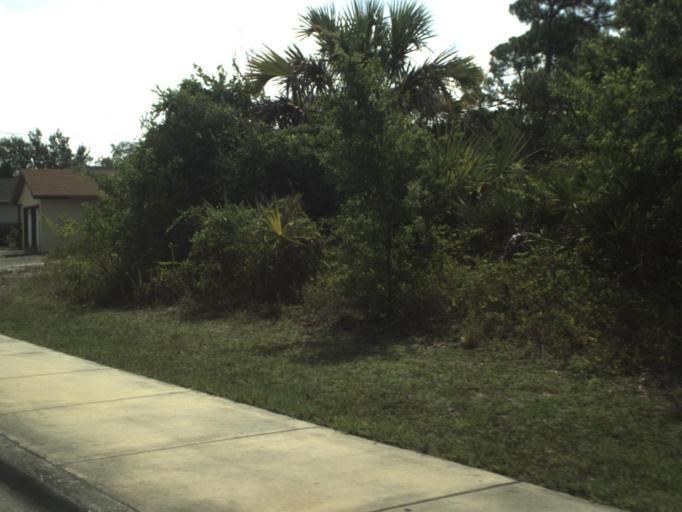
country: US
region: Florida
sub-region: Saint Lucie County
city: Port Saint Lucie
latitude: 27.2675
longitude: -80.3703
